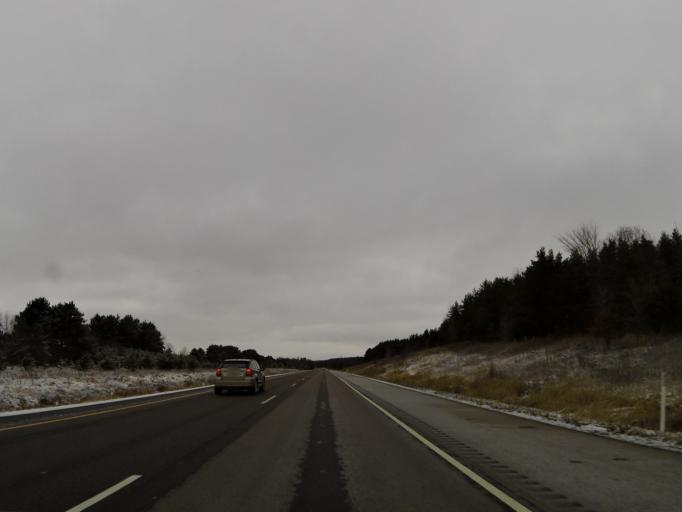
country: US
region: Wisconsin
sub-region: Trempealeau County
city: Osseo
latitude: 44.5556
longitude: -91.1728
